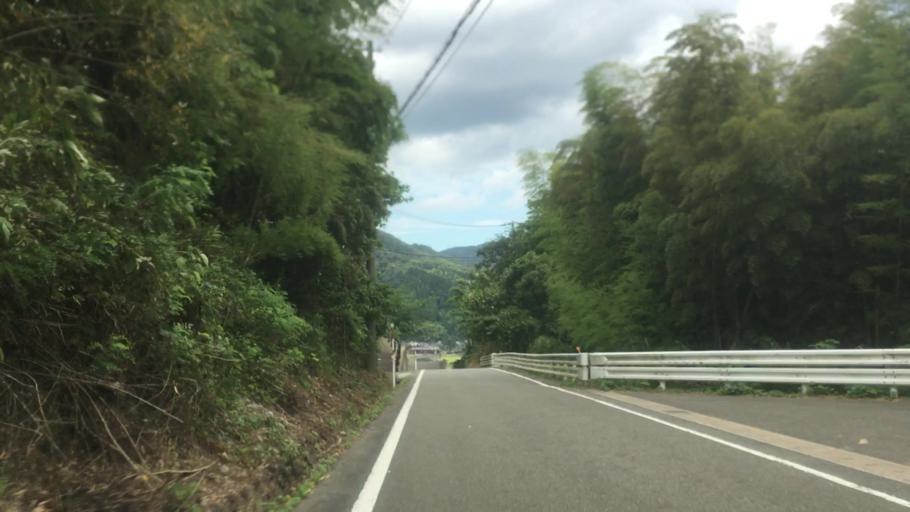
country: JP
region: Hyogo
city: Toyooka
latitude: 35.5854
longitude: 134.7993
